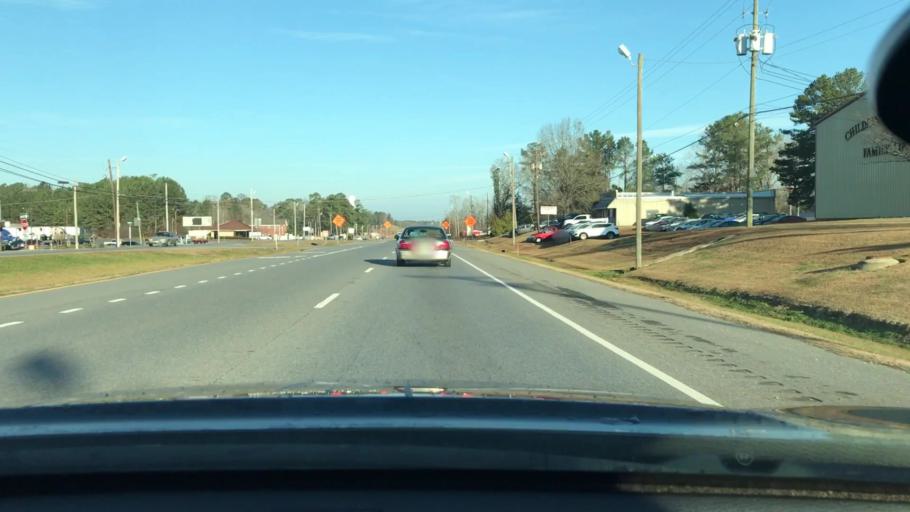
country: US
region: Alabama
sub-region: Talladega County
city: Childersburg
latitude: 33.2676
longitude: -86.3528
